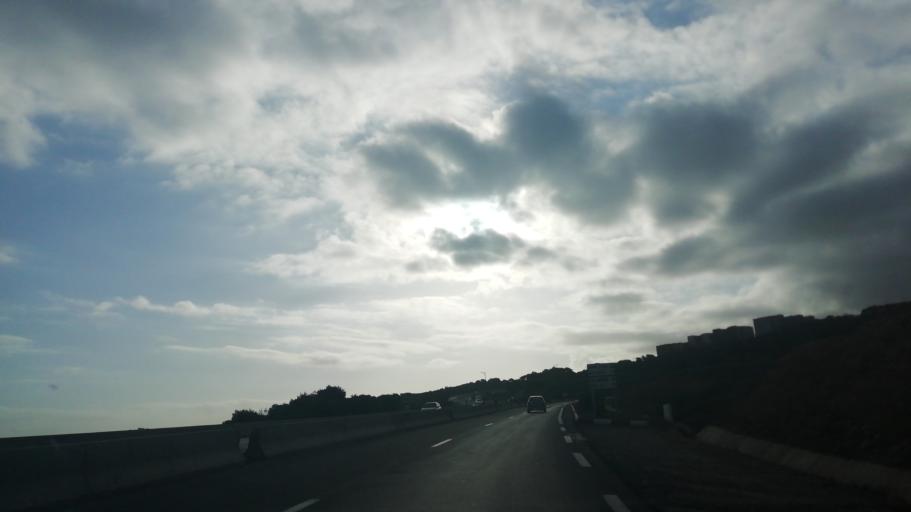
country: DZ
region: Mostaganem
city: Mostaganem
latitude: 36.1111
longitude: 0.2592
